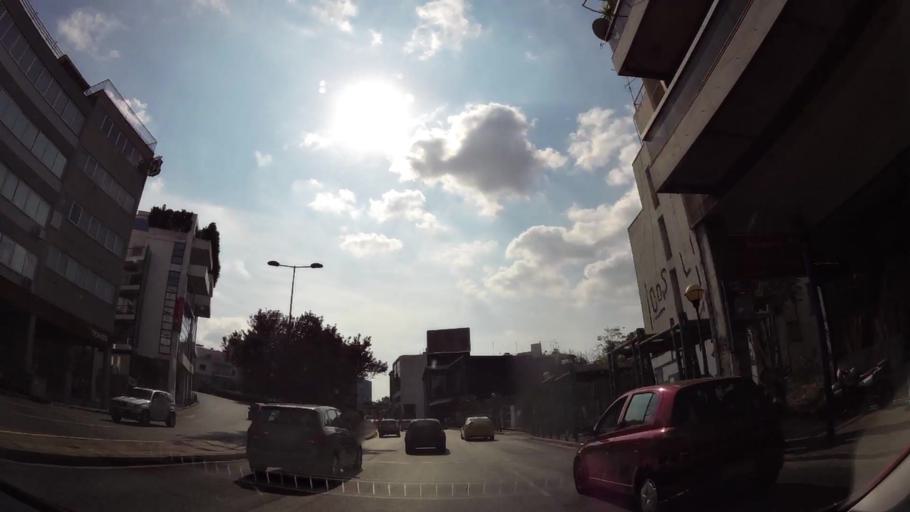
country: GR
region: Attica
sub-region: Nomarchia Athinas
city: Dhafni
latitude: 37.9667
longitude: 23.7332
